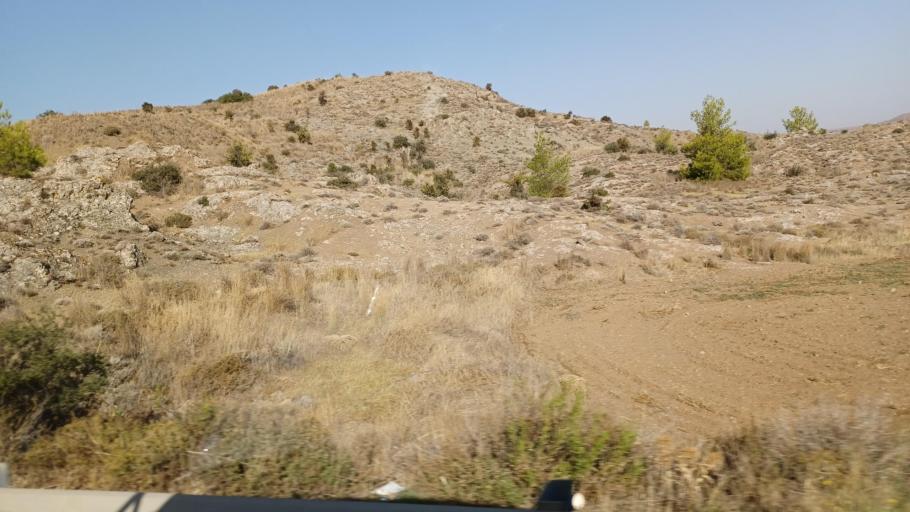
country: CY
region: Lefkosia
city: Lythrodontas
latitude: 34.9688
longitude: 33.3436
